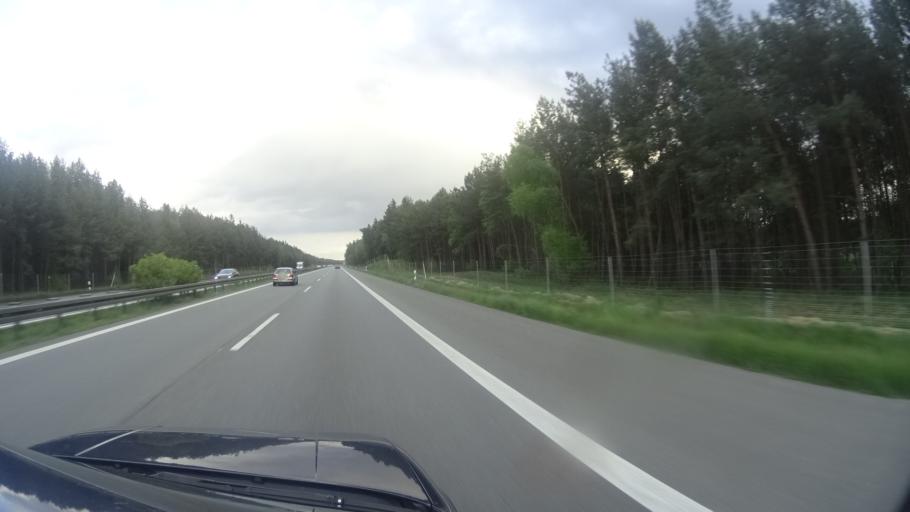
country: DE
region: Brandenburg
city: Wittstock
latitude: 53.1022
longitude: 12.4885
